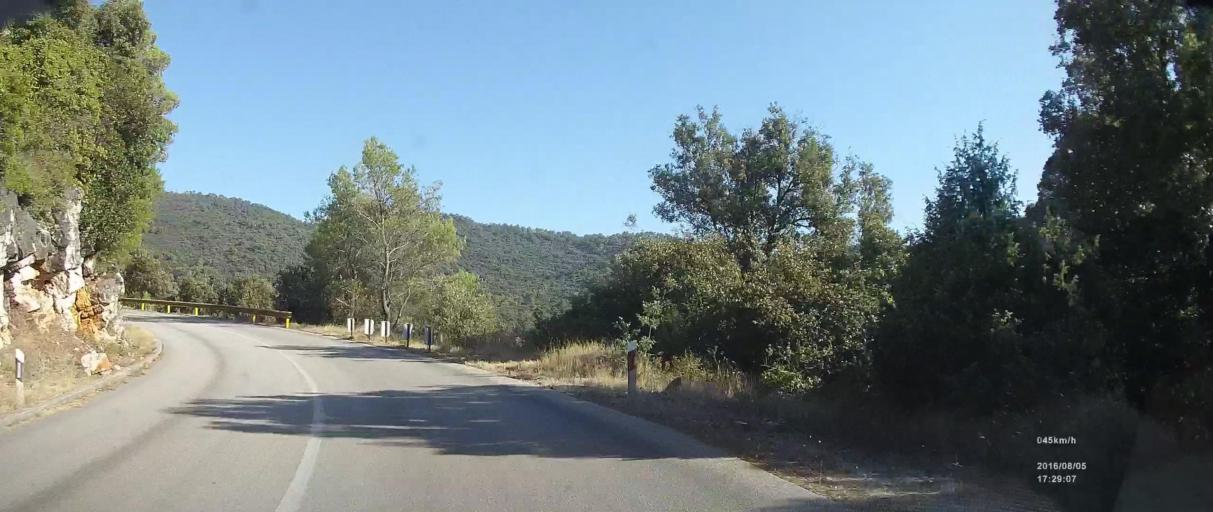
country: HR
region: Dubrovacko-Neretvanska
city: Blato
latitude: 42.7793
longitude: 17.4053
